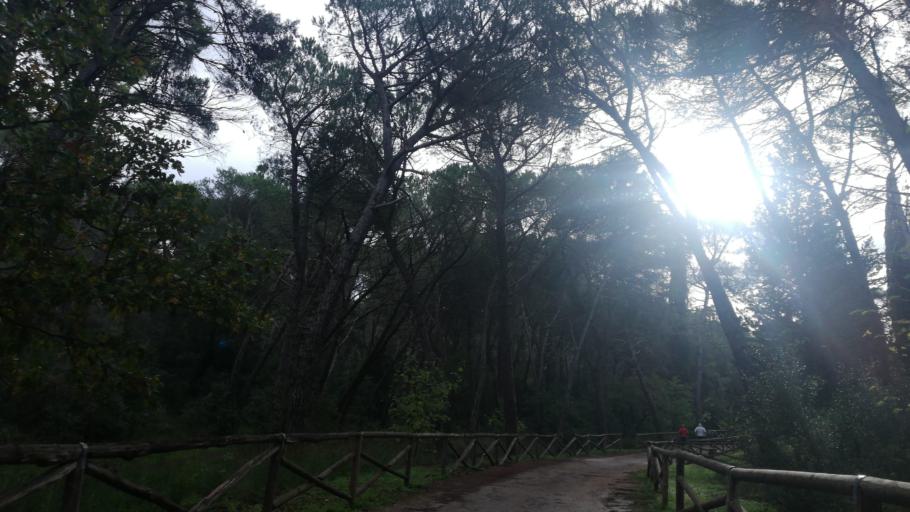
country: IT
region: Apulia
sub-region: Provincia di Bari
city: Cassano delle Murge
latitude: 40.8893
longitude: 16.7002
